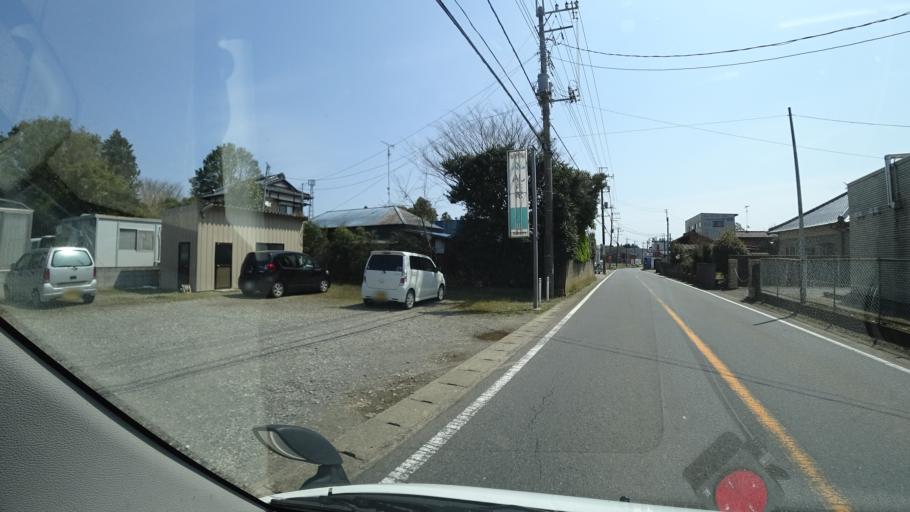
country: JP
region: Chiba
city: Narita
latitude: 35.7184
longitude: 140.3999
